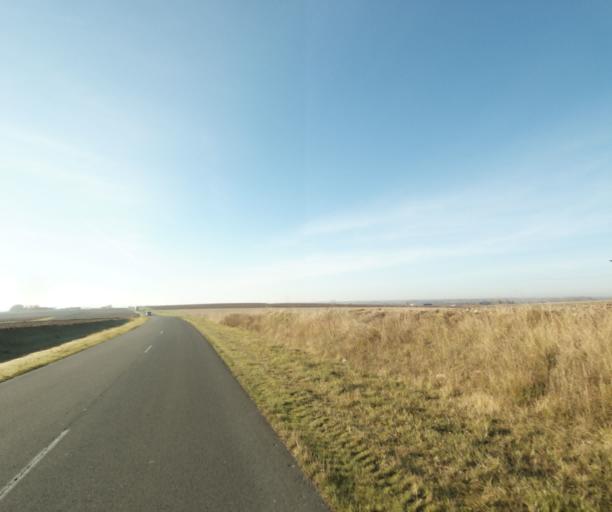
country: FR
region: Poitou-Charentes
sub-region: Departement de la Charente-Maritime
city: Cherac
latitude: 45.6966
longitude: -0.4482
